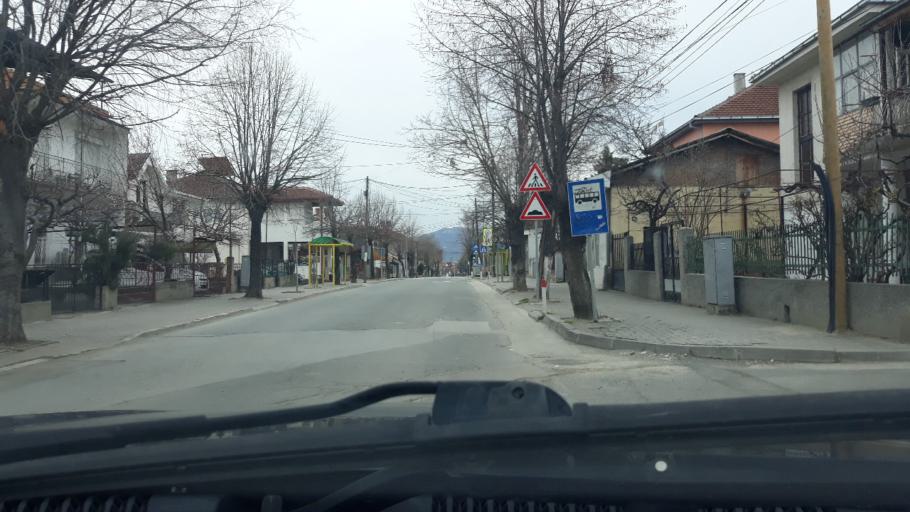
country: MK
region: Kavadarci
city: Kavadarci
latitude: 41.4323
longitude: 22.0082
